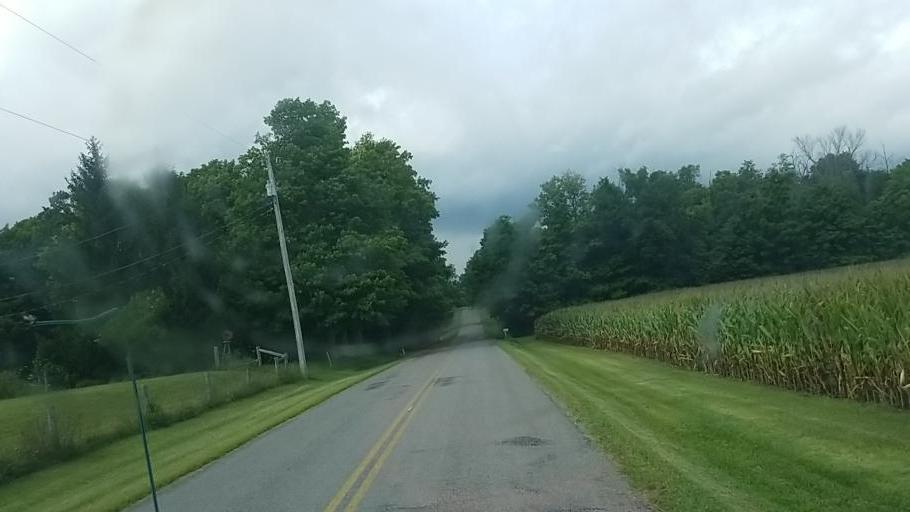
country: US
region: Ohio
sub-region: Logan County
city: West Liberty
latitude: 40.2548
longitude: -83.6550
